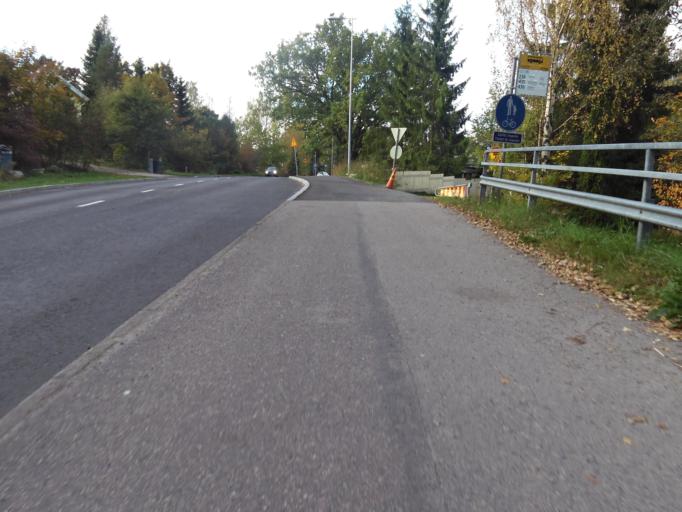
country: FI
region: Uusimaa
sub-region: Helsinki
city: Kilo
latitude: 60.2731
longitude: 24.7508
